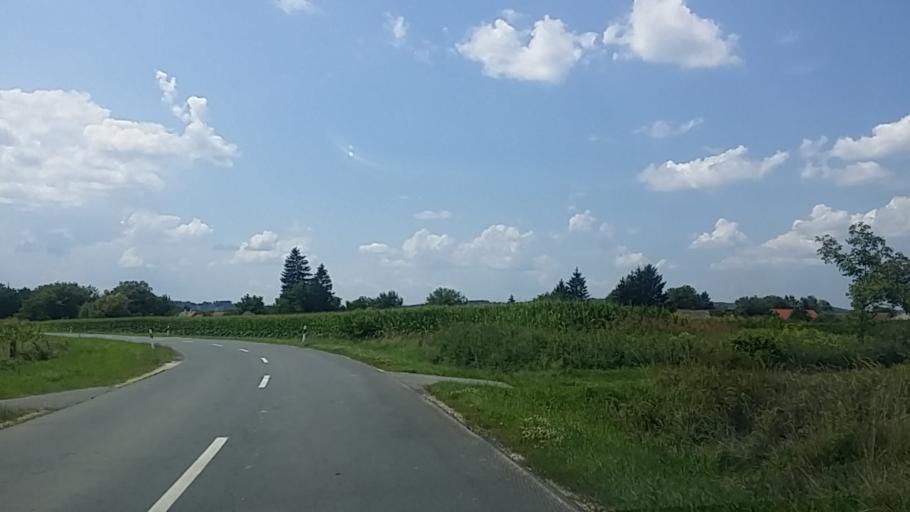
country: HR
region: Medimurska
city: Podturen
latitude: 46.5161
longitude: 16.5871
